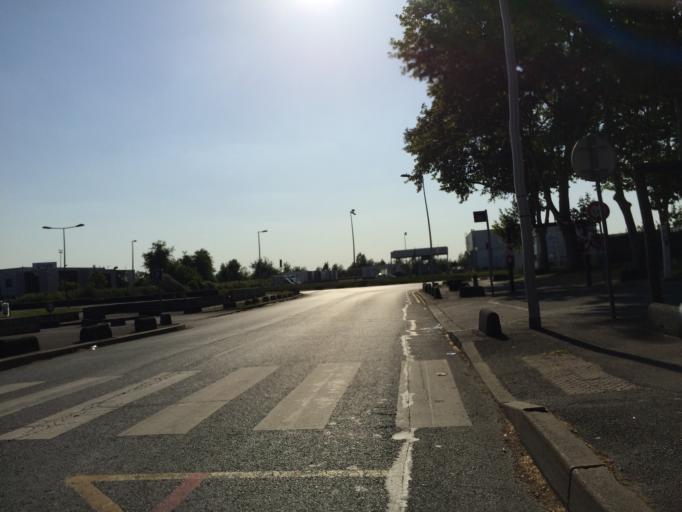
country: FR
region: Ile-de-France
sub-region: Departement de l'Essonne
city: Bondoufle
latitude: 48.6206
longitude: 2.3755
